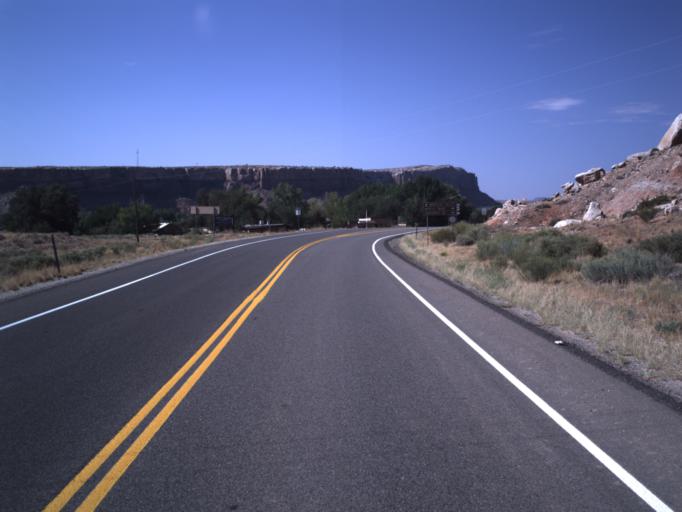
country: US
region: Utah
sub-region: San Juan County
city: Blanding
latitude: 37.2881
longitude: -109.5434
